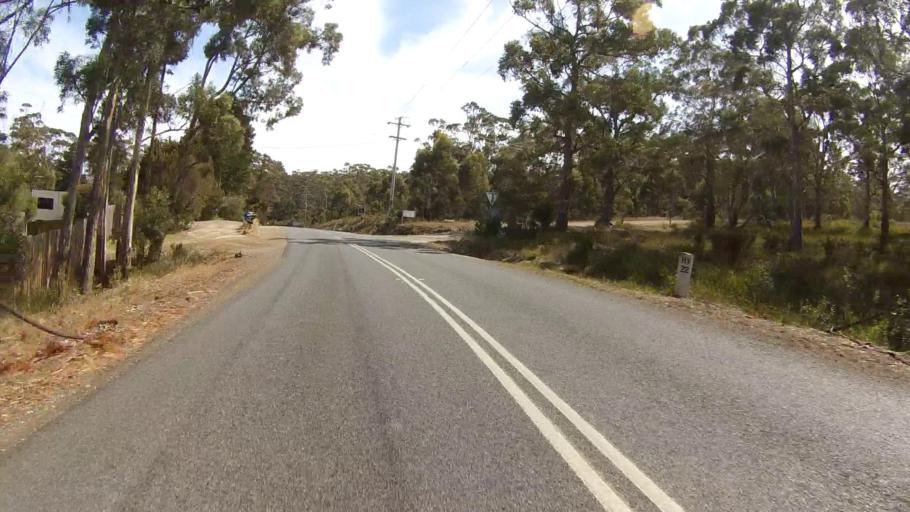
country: AU
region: Tasmania
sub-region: Huon Valley
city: Cygnet
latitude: -43.2697
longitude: 147.1476
